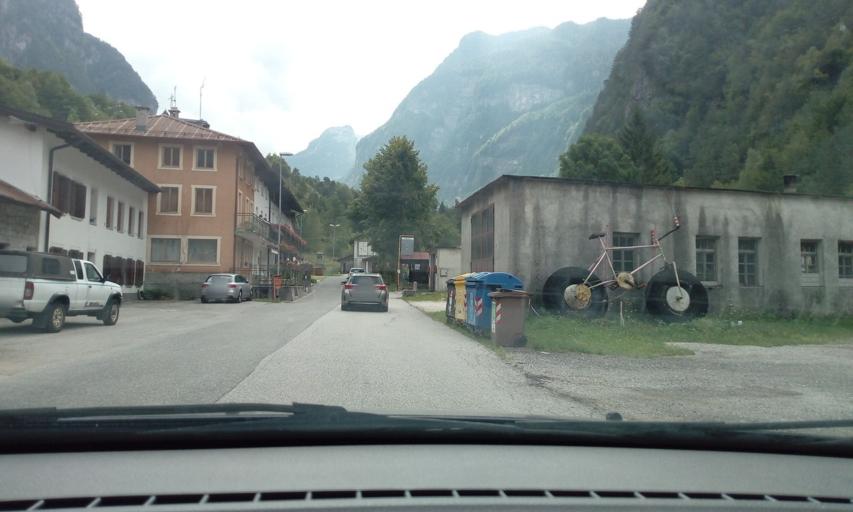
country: IT
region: Friuli Venezia Giulia
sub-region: Provincia di Udine
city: Malborghetto
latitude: 46.4014
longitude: 13.4183
